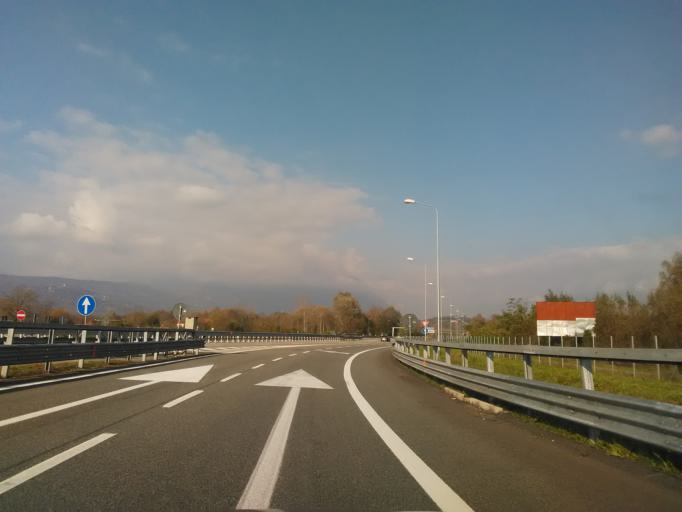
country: IT
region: Piedmont
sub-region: Provincia di Torino
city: Pavone Canavese
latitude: 45.4271
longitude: 7.8470
